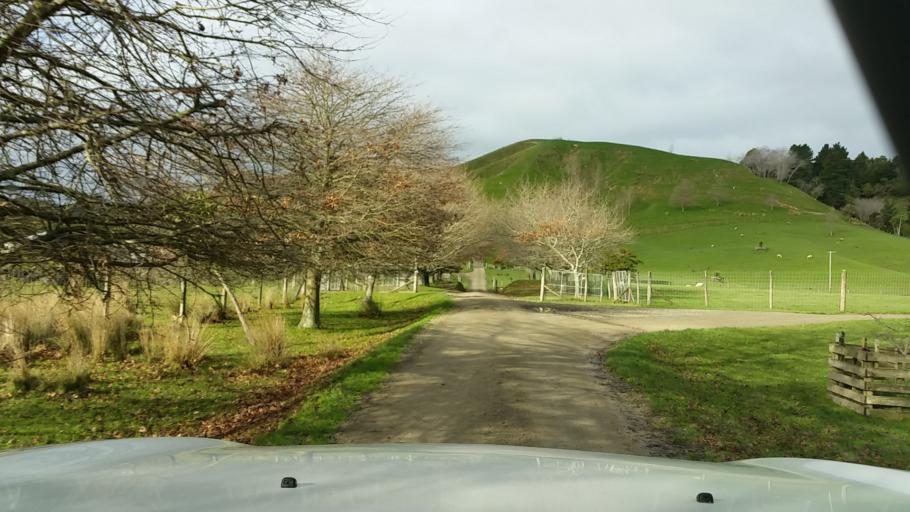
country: NZ
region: Wellington
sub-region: Masterton District
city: Masterton
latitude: -41.0470
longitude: 175.7293
